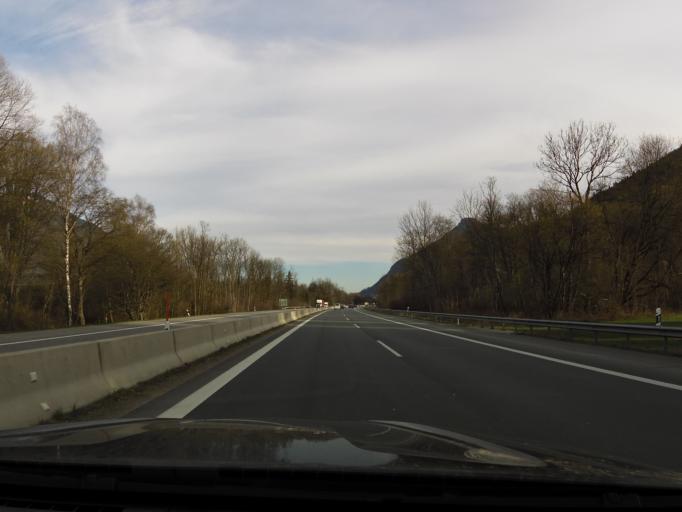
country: DE
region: Bavaria
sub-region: Upper Bavaria
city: Oberaudorf
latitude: 47.6549
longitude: 12.1854
